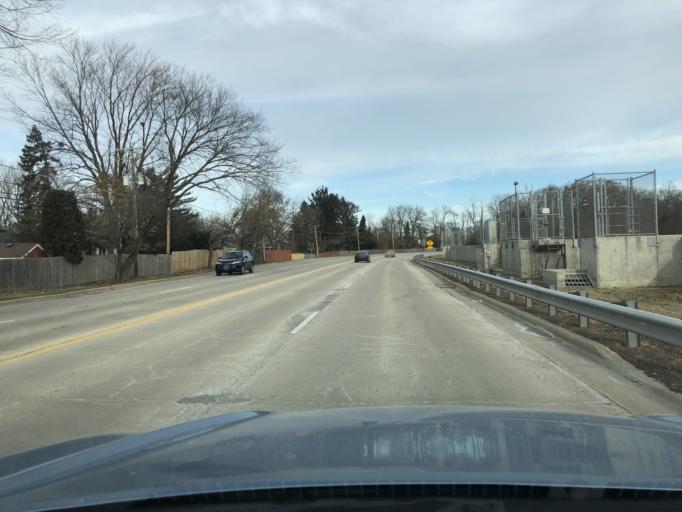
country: US
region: Illinois
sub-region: Cook County
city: Prospect Heights
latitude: 42.0994
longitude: -87.8902
